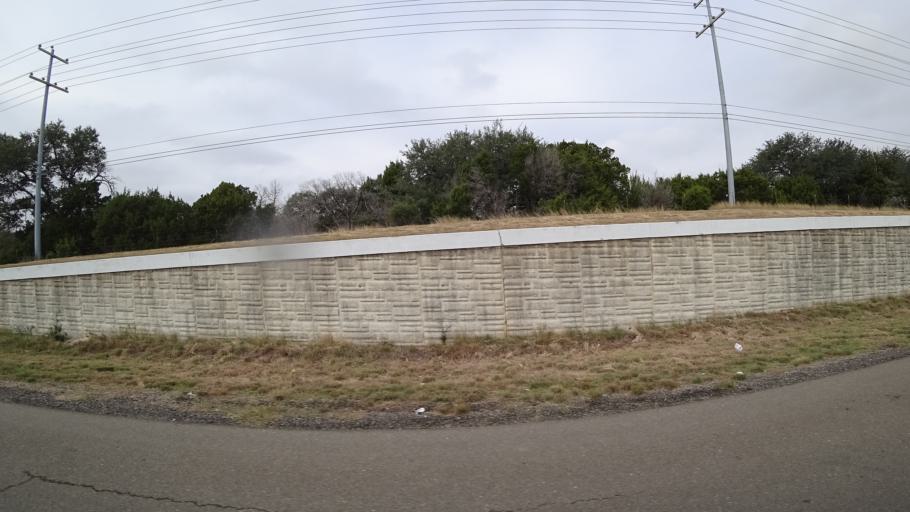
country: US
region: Texas
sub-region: Williamson County
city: Brushy Creek
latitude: 30.5109
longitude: -97.7746
